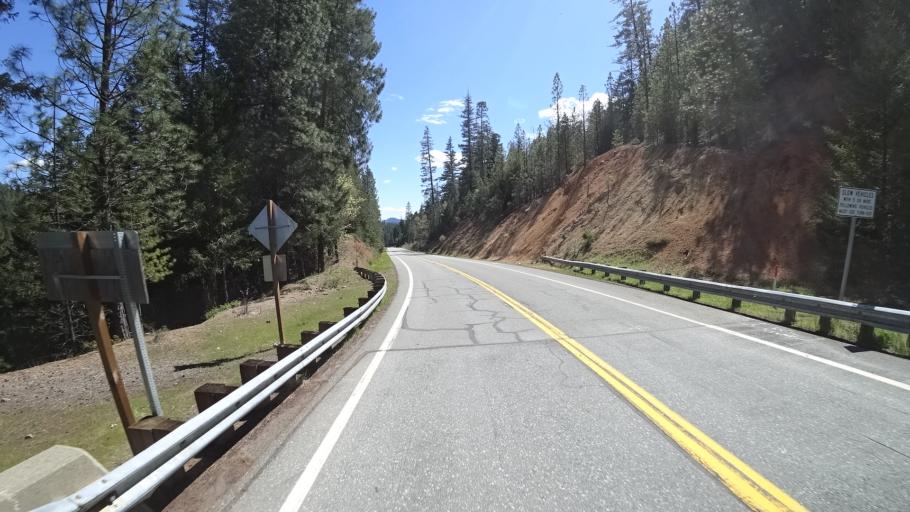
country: US
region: California
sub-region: Trinity County
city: Lewiston
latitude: 40.8745
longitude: -122.8026
